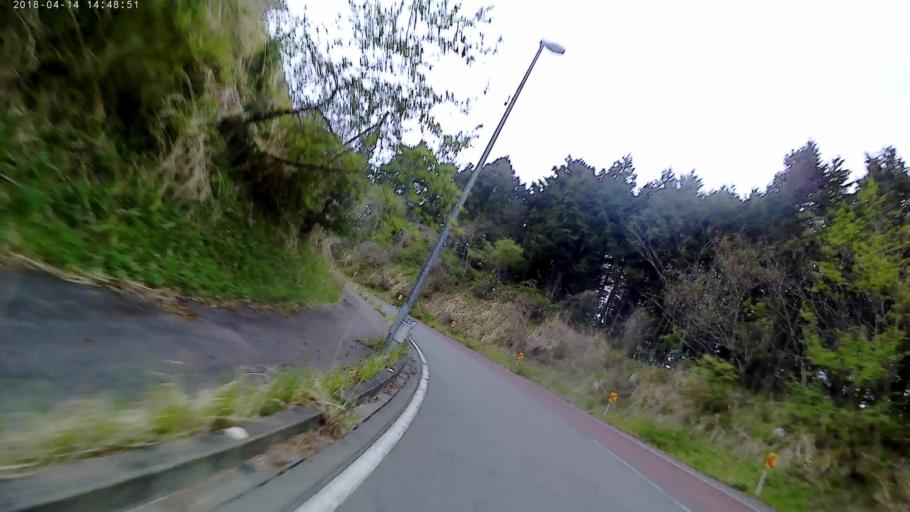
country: JP
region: Shizuoka
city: Gotemba
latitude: 35.3641
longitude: 138.9786
